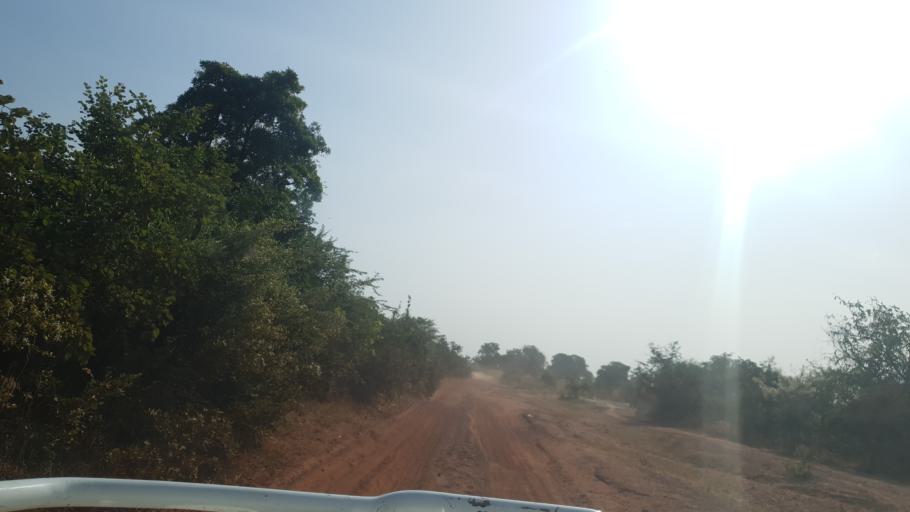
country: ML
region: Koulikoro
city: Dioila
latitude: 12.7080
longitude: -6.7779
